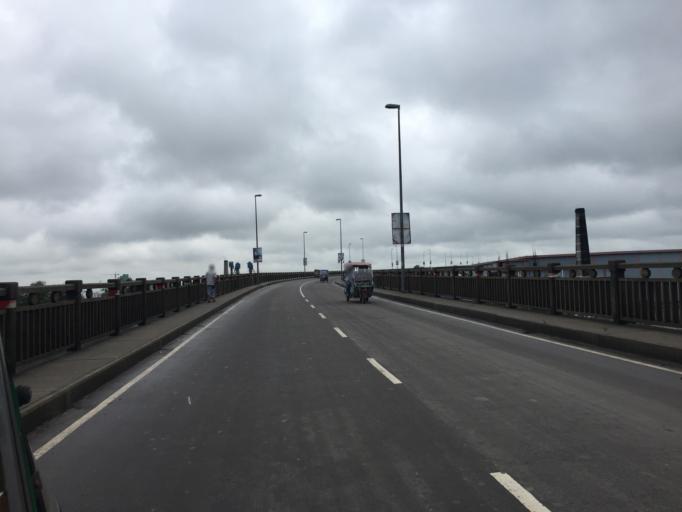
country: BD
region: Dhaka
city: Narayanganj
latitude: 23.5650
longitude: 90.5103
